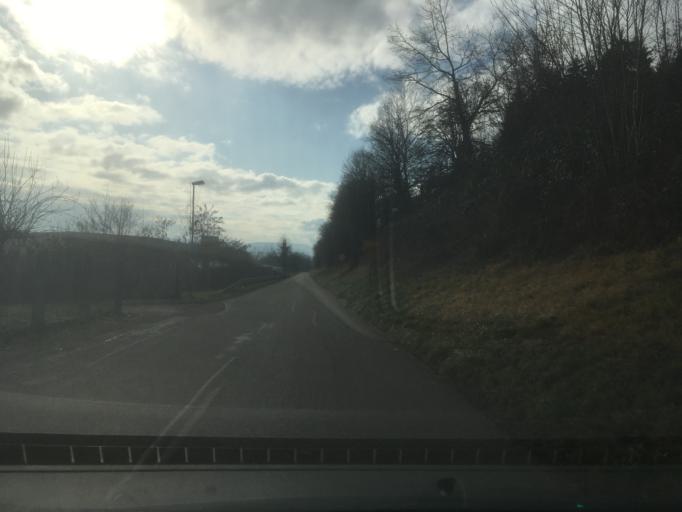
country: CH
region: Aargau
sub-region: Bezirk Zurzach
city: Koblenz
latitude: 47.6168
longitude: 8.2380
